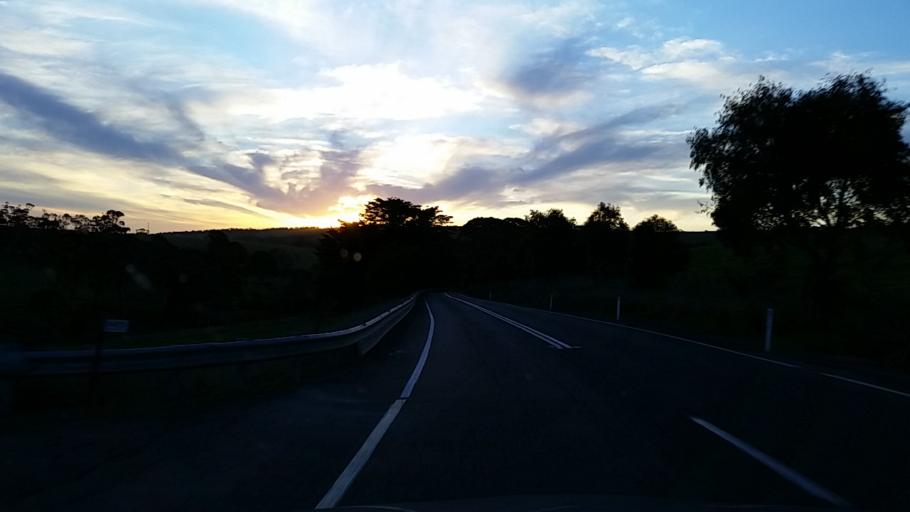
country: AU
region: South Australia
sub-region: Yankalilla
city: Normanville
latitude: -35.4229
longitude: 138.4119
